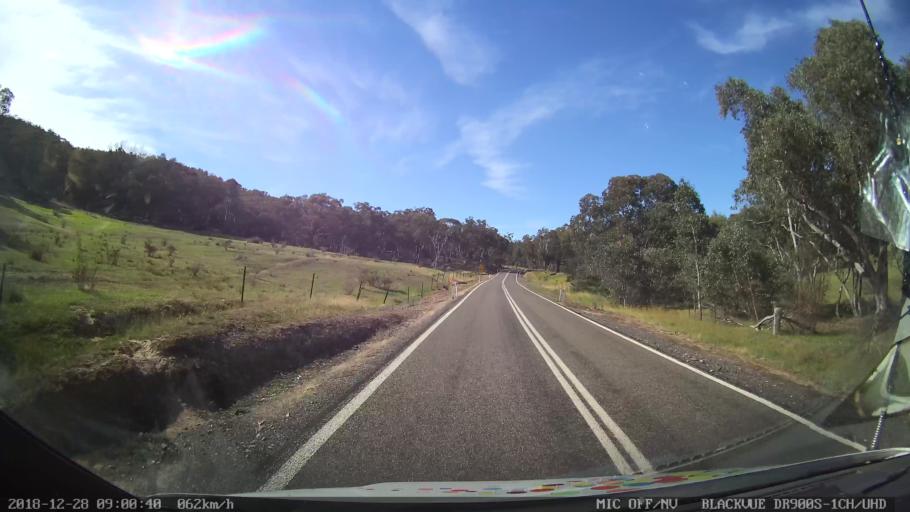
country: AU
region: New South Wales
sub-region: Upper Lachlan Shire
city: Crookwell
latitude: -34.1404
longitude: 149.3348
